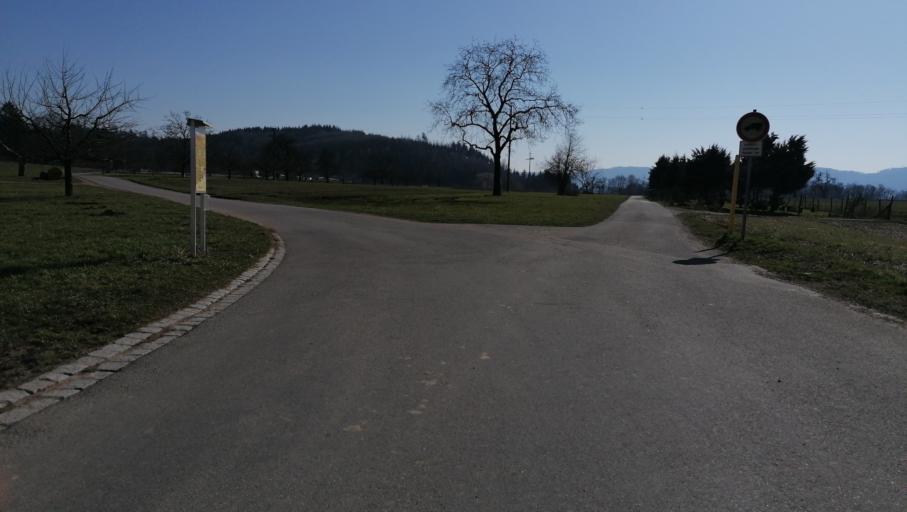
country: DE
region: Baden-Wuerttemberg
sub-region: Freiburg Region
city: Schworstadt
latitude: 47.5863
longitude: 7.9170
